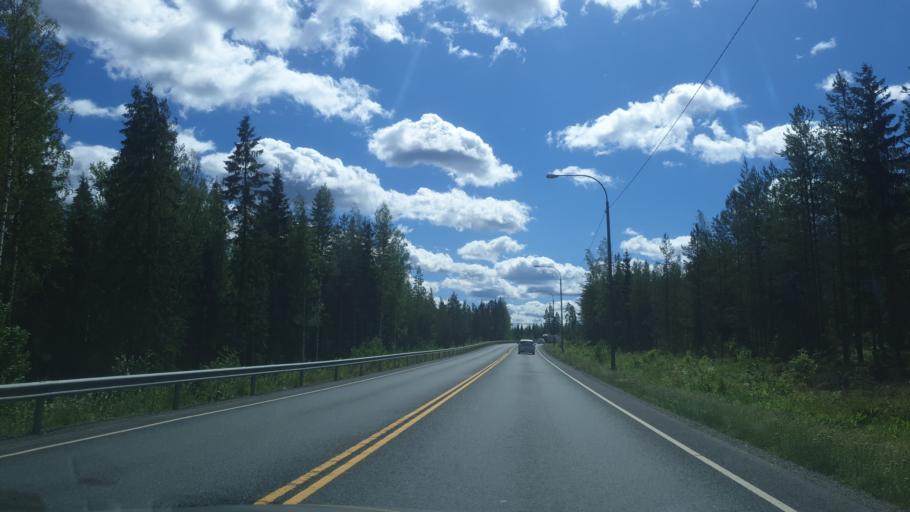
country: FI
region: Northern Savo
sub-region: Varkaus
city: Leppaevirta
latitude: 62.6282
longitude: 27.6194
